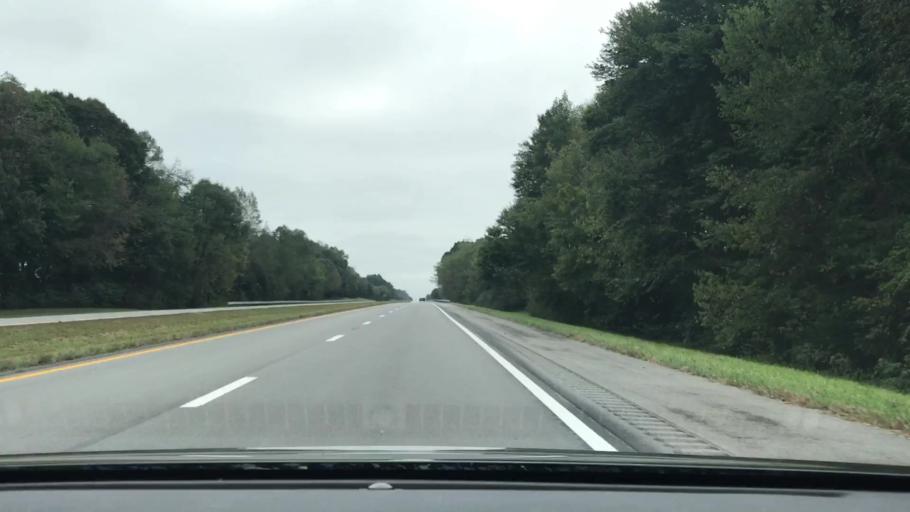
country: US
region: Kentucky
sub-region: Adair County
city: Columbia
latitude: 37.0782
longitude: -85.2377
